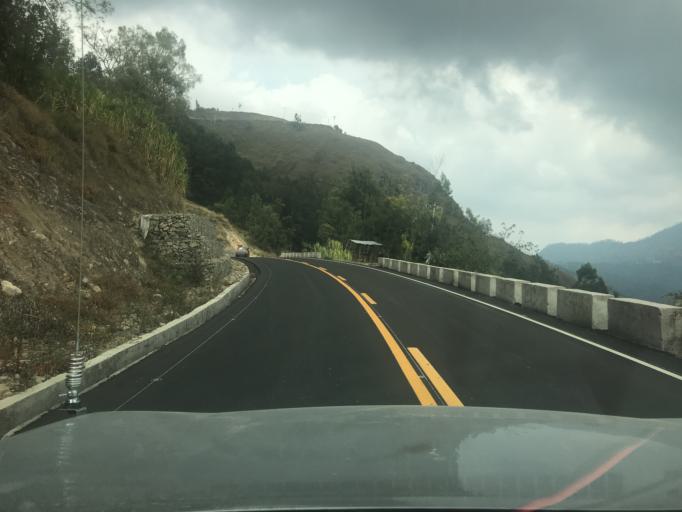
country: TL
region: Manufahi
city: Same
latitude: -8.8930
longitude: 125.5925
